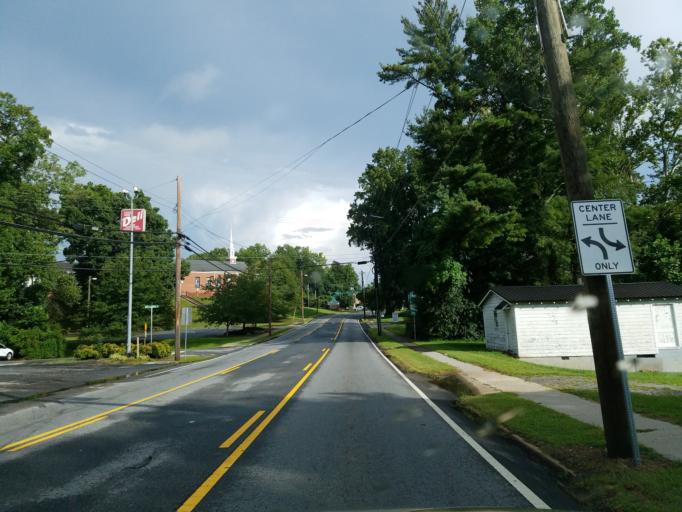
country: US
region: Georgia
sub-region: White County
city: Cleveland
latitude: 34.6008
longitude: -83.7645
